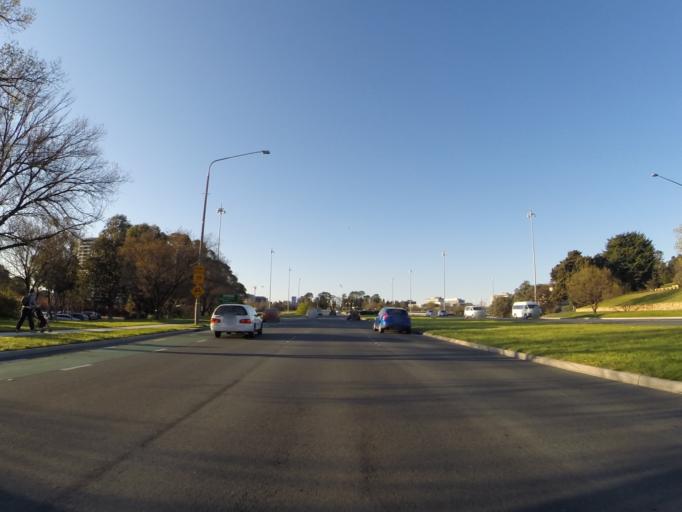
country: AU
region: Australian Capital Territory
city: Canberra
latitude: -35.2875
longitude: 149.1276
